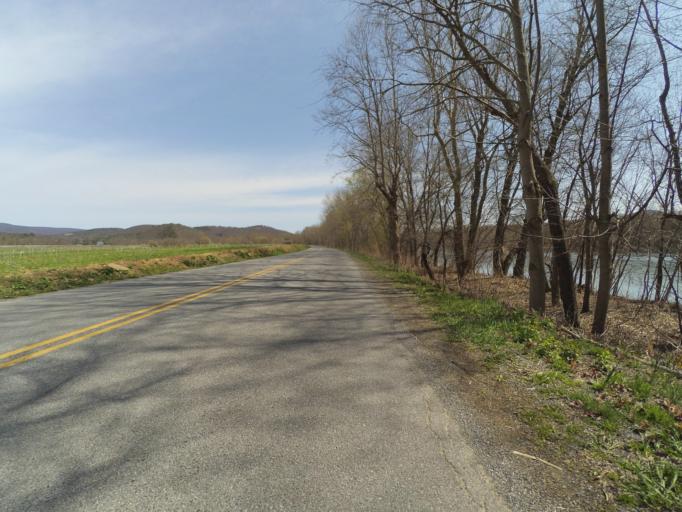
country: US
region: Pennsylvania
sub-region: Clinton County
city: Dunnstown
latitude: 41.1630
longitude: -77.3716
